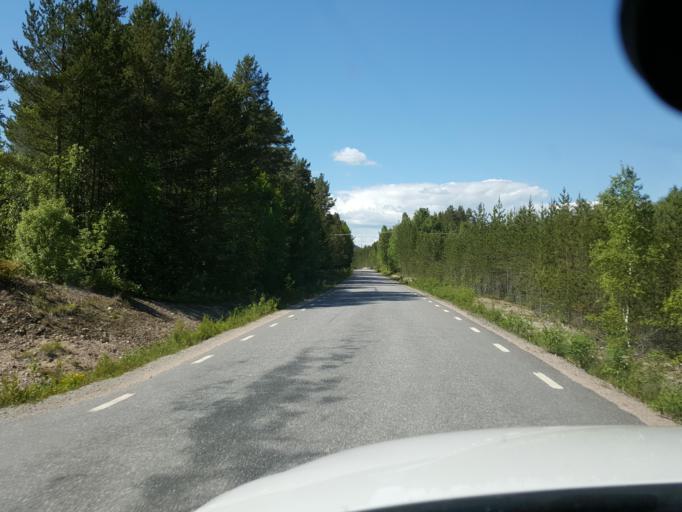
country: SE
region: Gaevleborg
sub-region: Ljusdals Kommun
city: Jaervsoe
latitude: 61.7601
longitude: 16.2270
